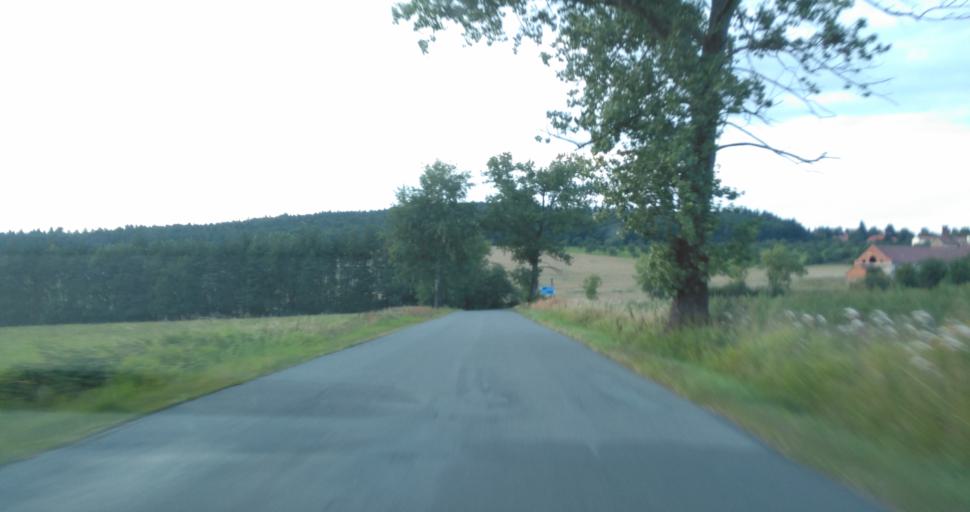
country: CZ
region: Plzensky
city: Zbiroh
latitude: 49.8504
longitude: 13.7450
